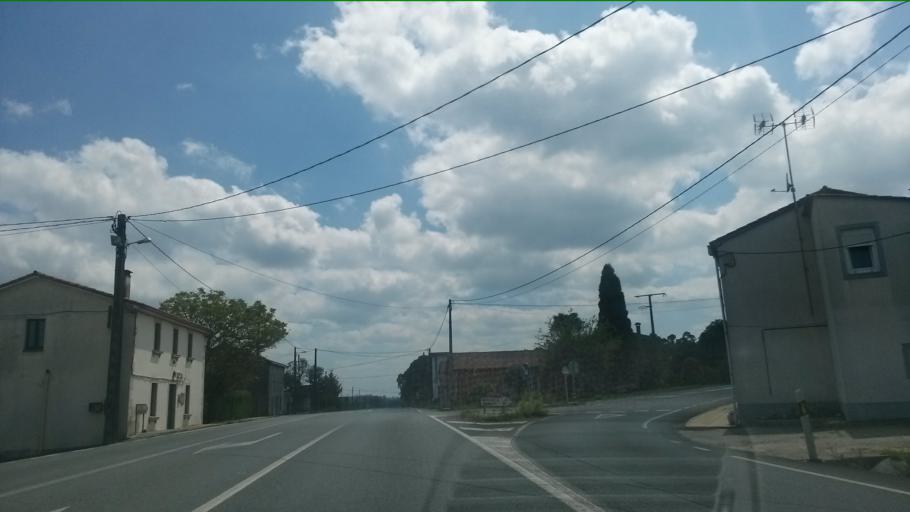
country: ES
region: Galicia
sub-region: Provincia da Coruna
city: Mesia
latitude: 43.0723
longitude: -8.1990
